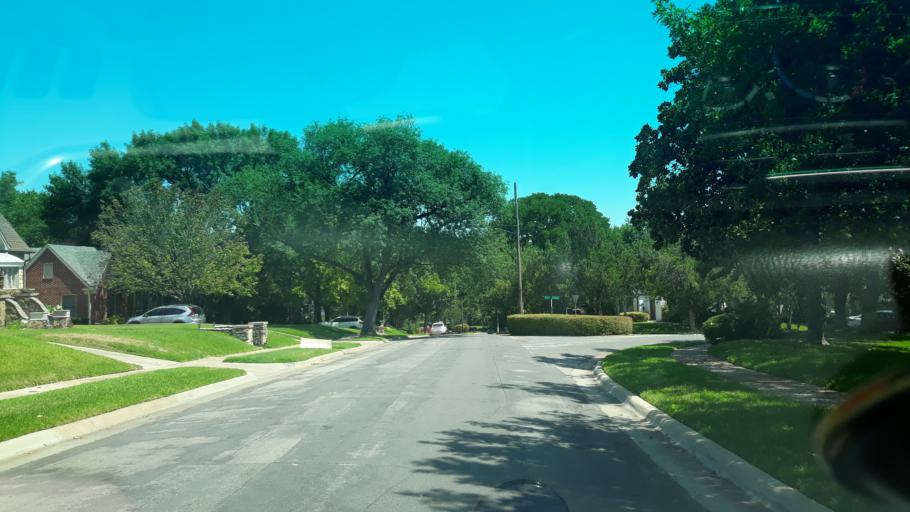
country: US
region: Texas
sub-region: Dallas County
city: Highland Park
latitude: 32.8168
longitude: -96.7399
